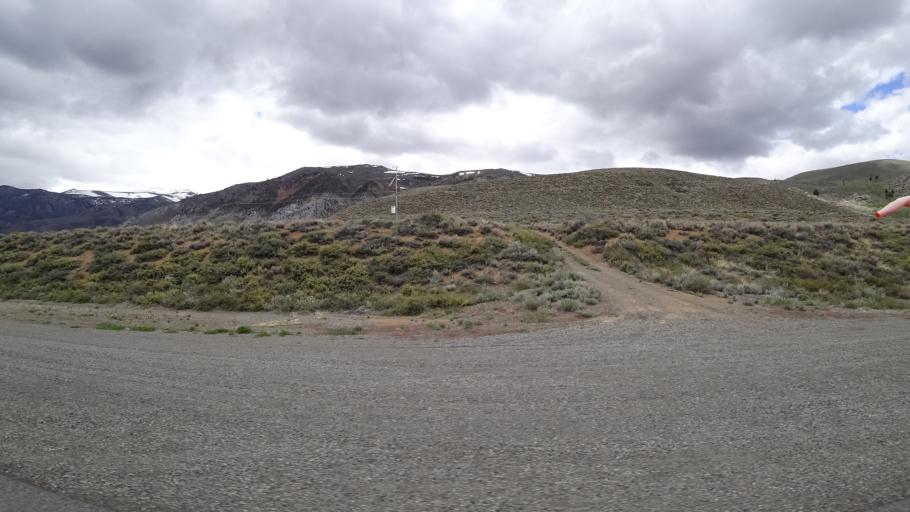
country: US
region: California
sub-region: Mono County
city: Bridgeport
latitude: 38.0585
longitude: -119.1669
